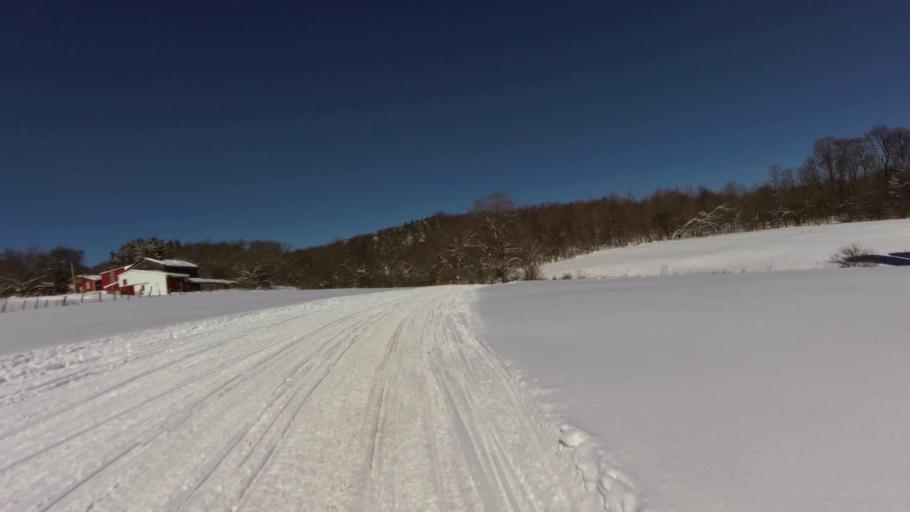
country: US
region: New York
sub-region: Chautauqua County
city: Mayville
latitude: 42.2525
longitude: -79.4409
